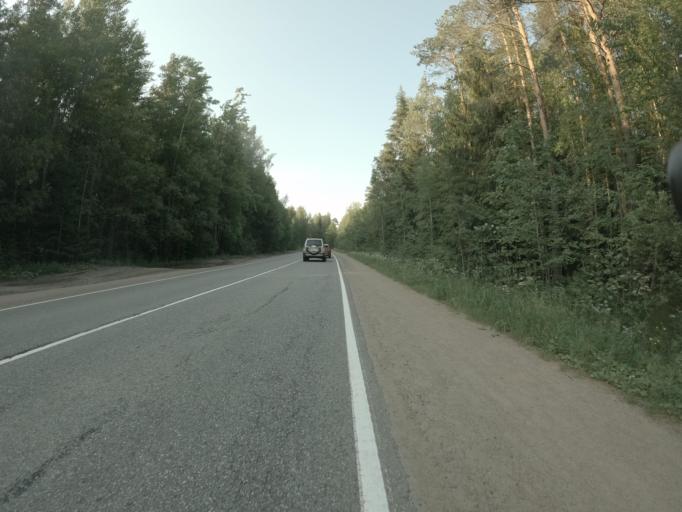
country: RU
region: Leningrad
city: Veshchevo
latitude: 60.4707
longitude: 29.2569
